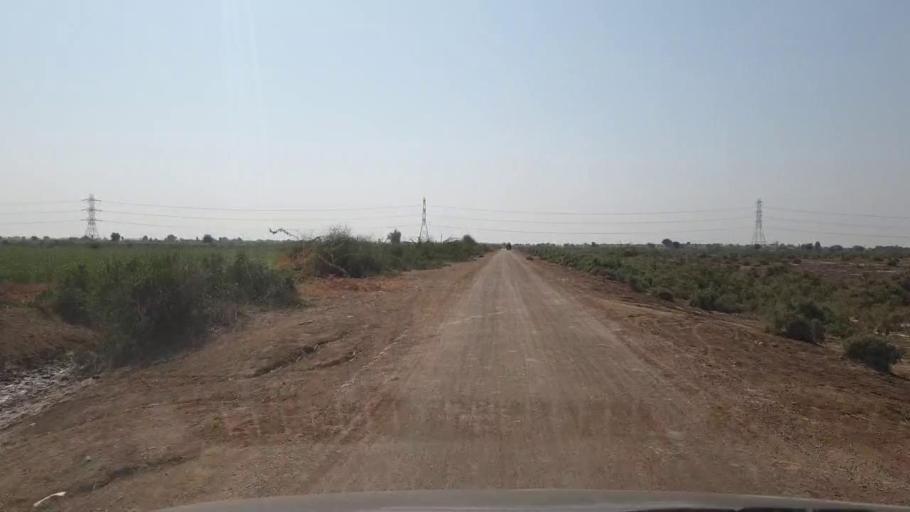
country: PK
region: Sindh
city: Digri
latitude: 25.1917
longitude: 69.2233
